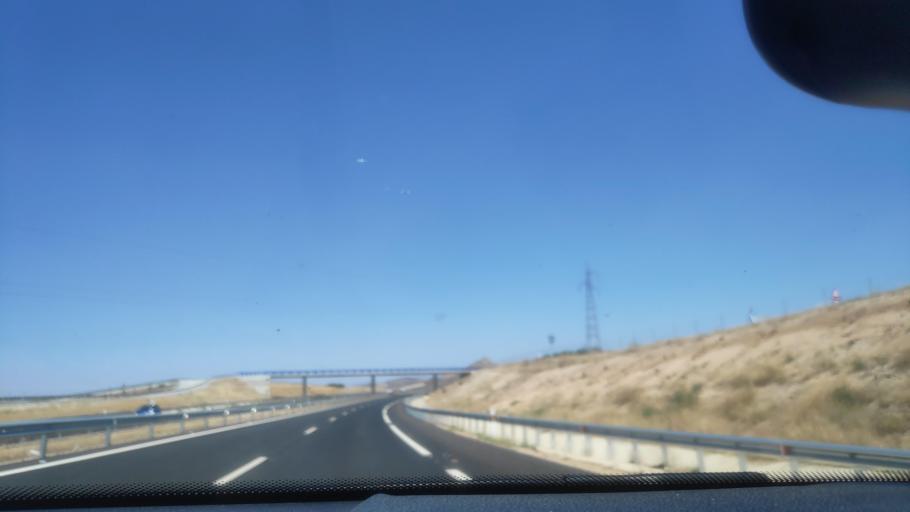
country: ES
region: Andalusia
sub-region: Provincia de Granada
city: Otura
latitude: 37.0723
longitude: -3.6588
